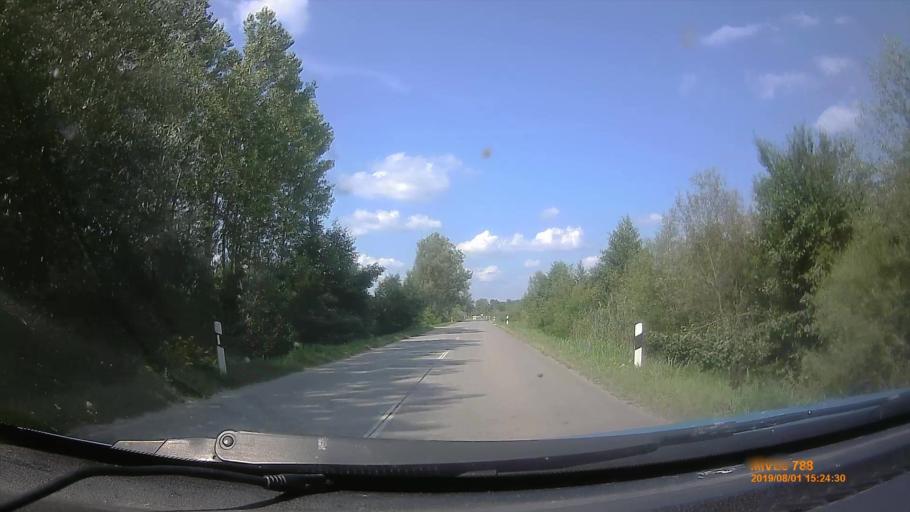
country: HU
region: Baranya
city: Sellye
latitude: 45.8850
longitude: 17.8515
